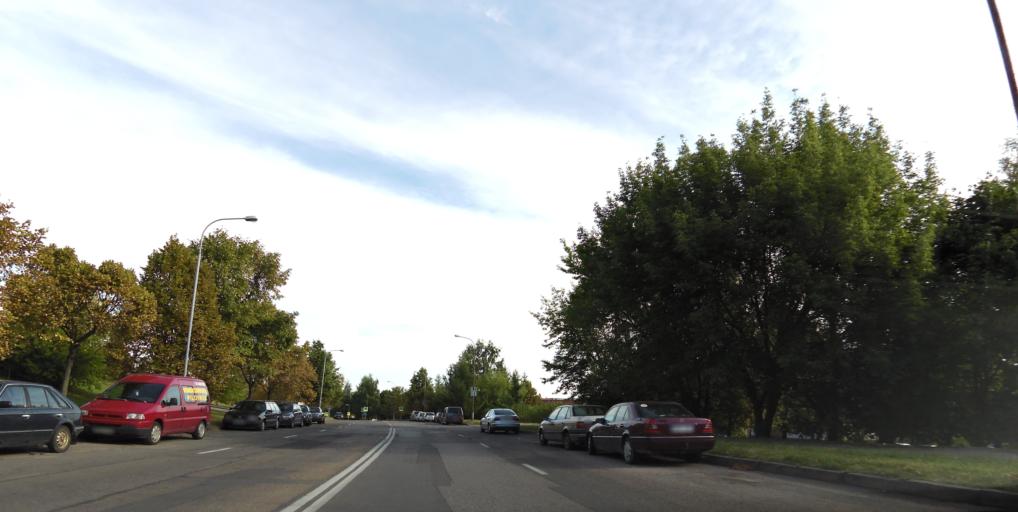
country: LT
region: Vilnius County
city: Seskine
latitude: 54.7132
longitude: 25.2515
